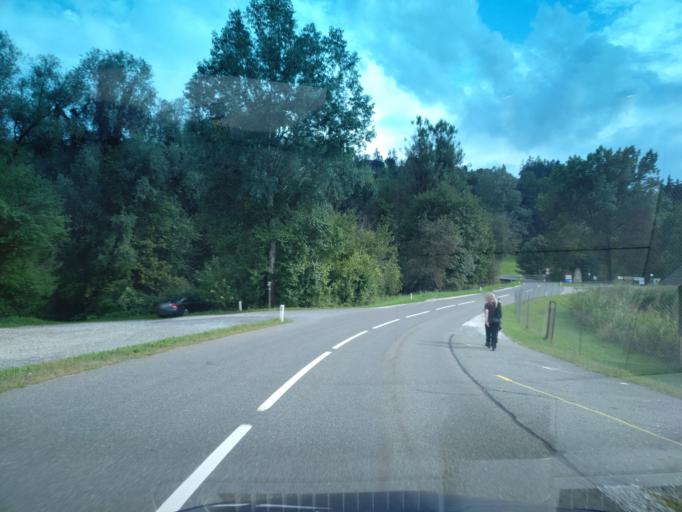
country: AT
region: Styria
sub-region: Politischer Bezirk Leibnitz
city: Seggauberg
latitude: 46.7784
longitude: 15.5193
